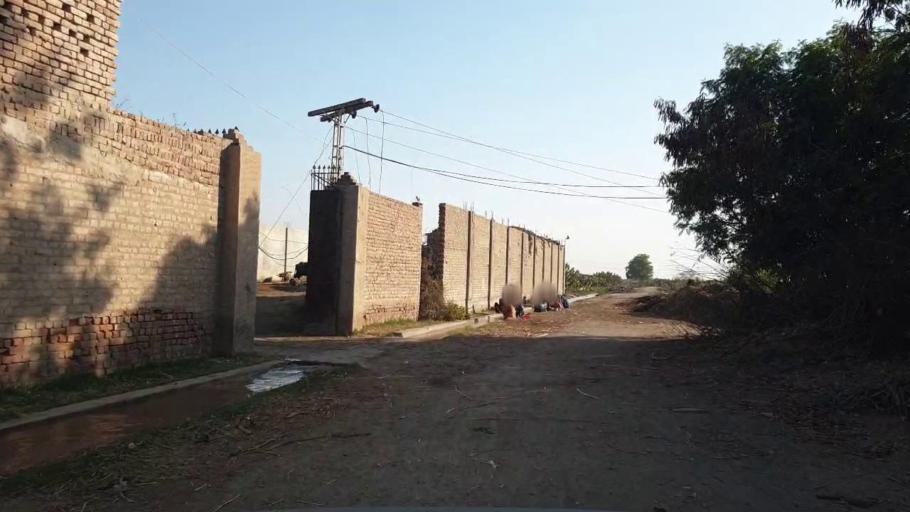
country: PK
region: Sindh
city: Tando Allahyar
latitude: 25.3466
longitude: 68.6818
